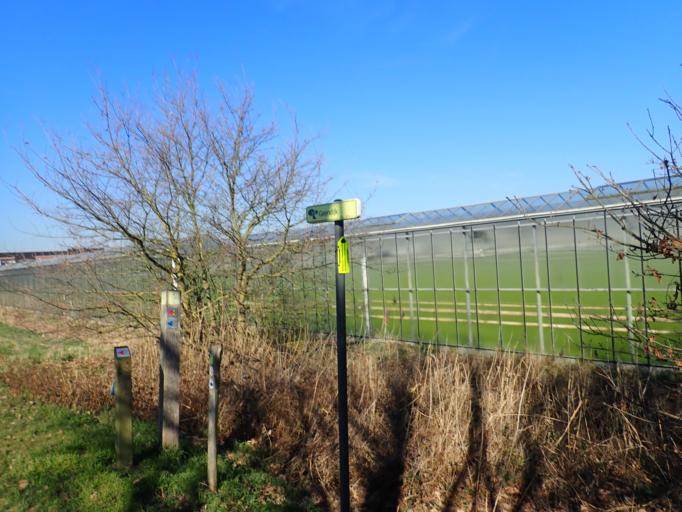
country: BE
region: Flanders
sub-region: Provincie Oost-Vlaanderen
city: Hamme
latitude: 51.0647
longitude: 4.1608
